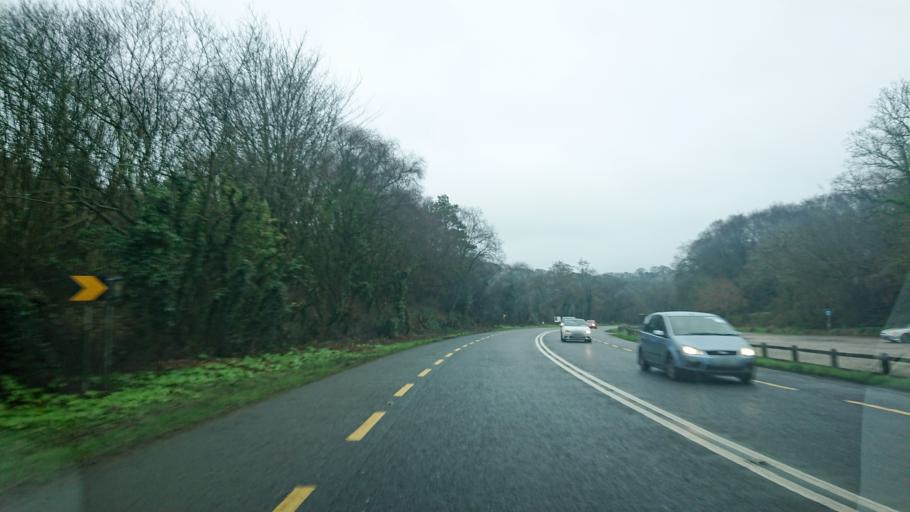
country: IE
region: Munster
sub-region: County Cork
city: Bandon
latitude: 51.7689
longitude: -8.6899
